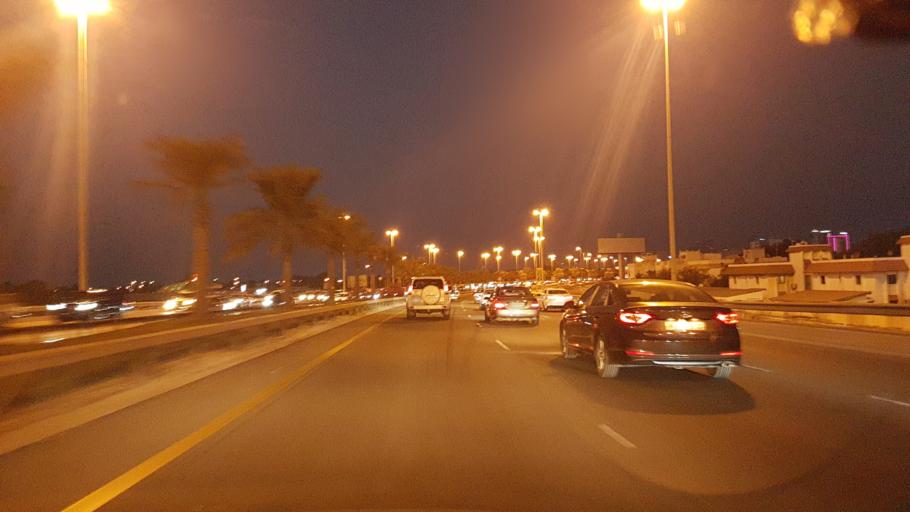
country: BH
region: Manama
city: Jidd Hafs
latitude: 26.2199
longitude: 50.5218
